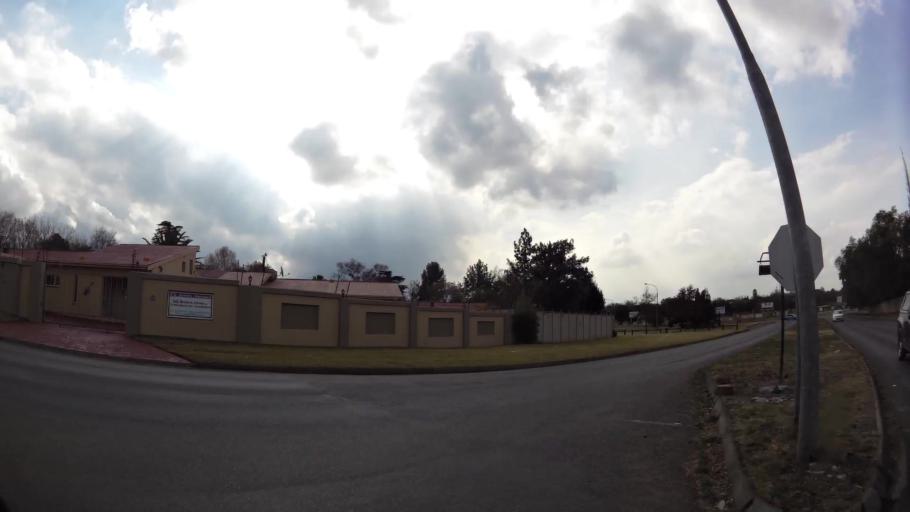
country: ZA
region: Gauteng
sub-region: Sedibeng District Municipality
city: Vanderbijlpark
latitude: -26.7324
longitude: 27.8314
